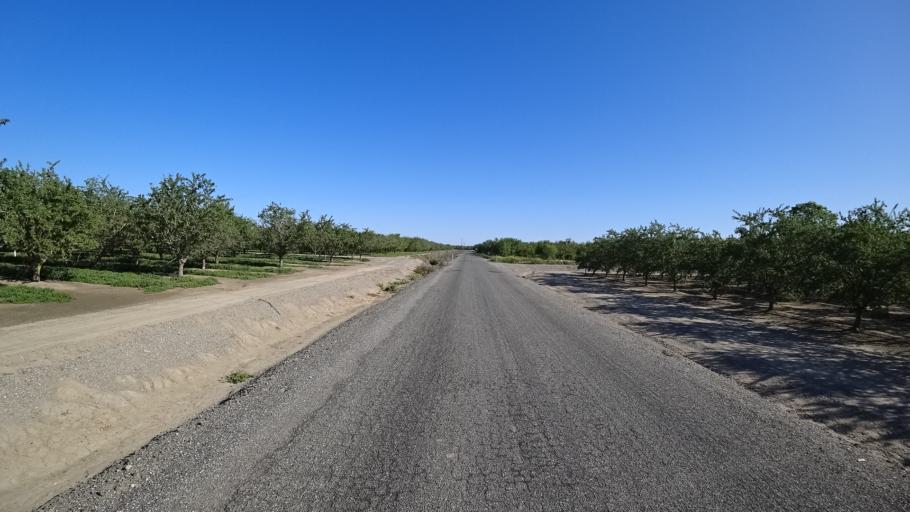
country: US
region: California
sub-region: Glenn County
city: Hamilton City
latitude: 39.7051
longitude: -122.0642
